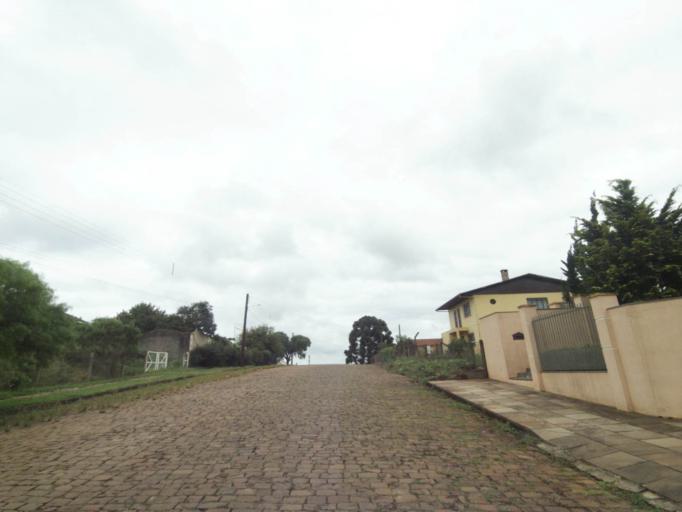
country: BR
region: Rio Grande do Sul
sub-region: Lagoa Vermelha
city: Lagoa Vermelha
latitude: -28.2132
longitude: -51.5302
